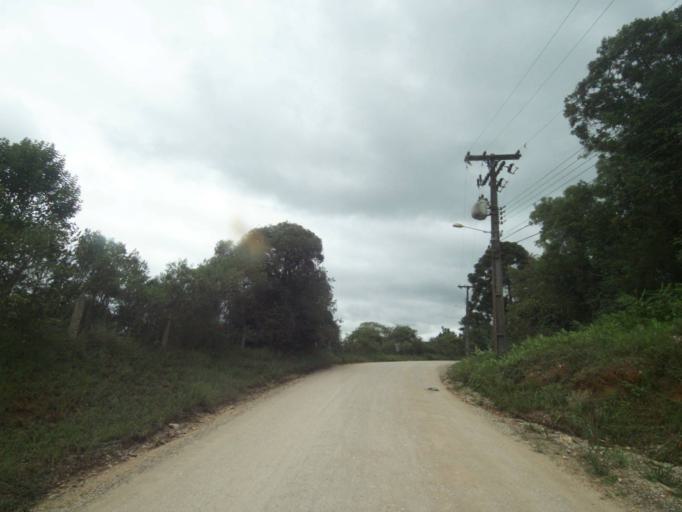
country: BR
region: Parana
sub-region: Campina Grande Do Sul
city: Campina Grande do Sul
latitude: -25.3233
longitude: -49.0833
